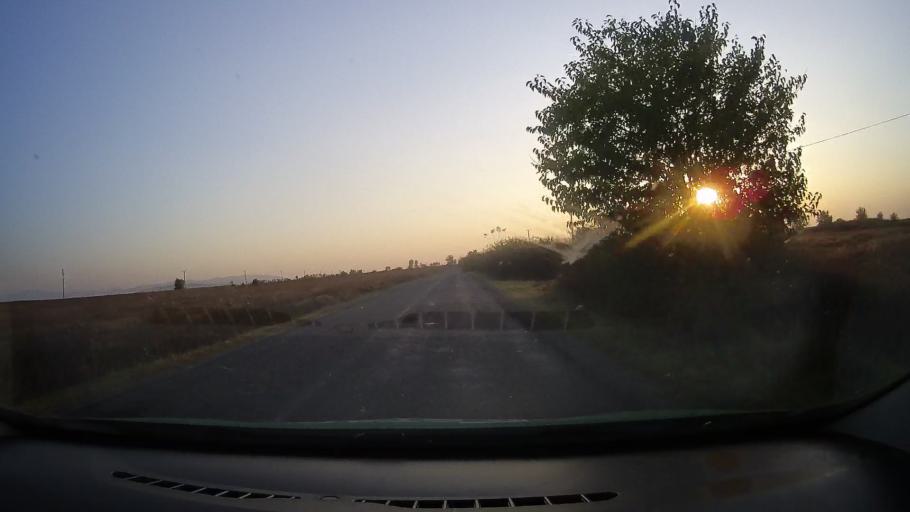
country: RO
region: Arad
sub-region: Comuna Sicula
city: Sicula
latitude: 46.4260
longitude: 21.7519
